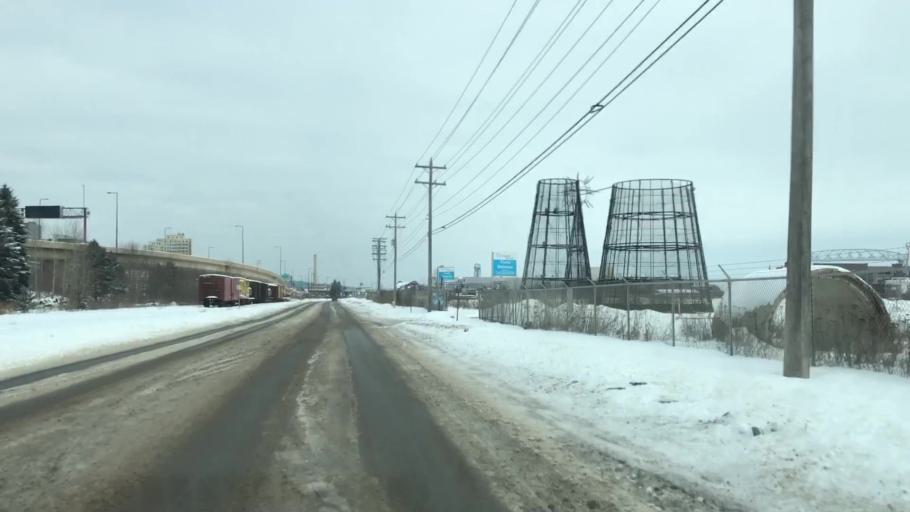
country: US
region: Minnesota
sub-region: Saint Louis County
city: Duluth
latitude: 46.7757
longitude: -92.1087
